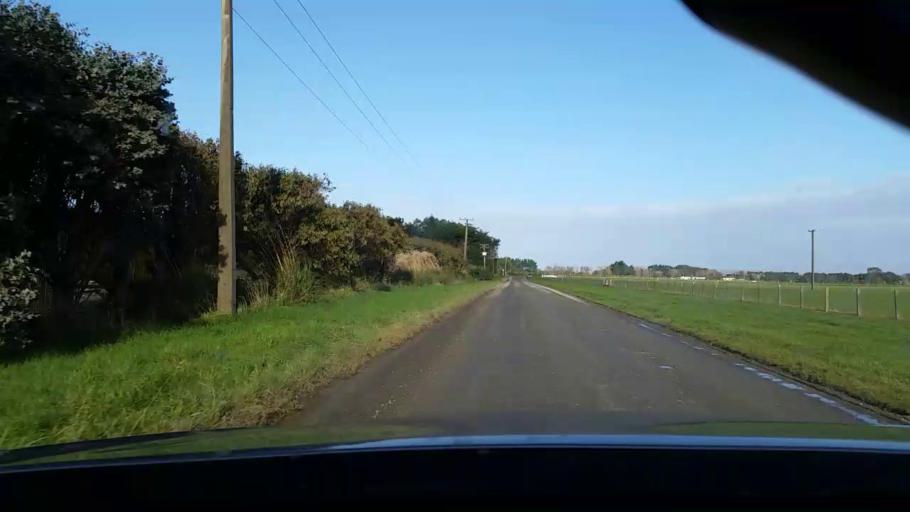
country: NZ
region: Southland
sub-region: Invercargill City
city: Invercargill
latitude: -46.3070
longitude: 168.3033
